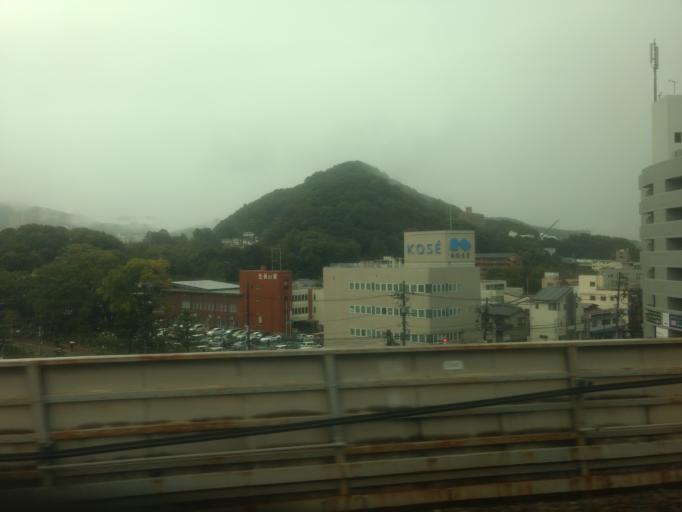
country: JP
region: Hiroshima
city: Hiroshima-shi
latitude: 34.4035
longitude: 132.4687
